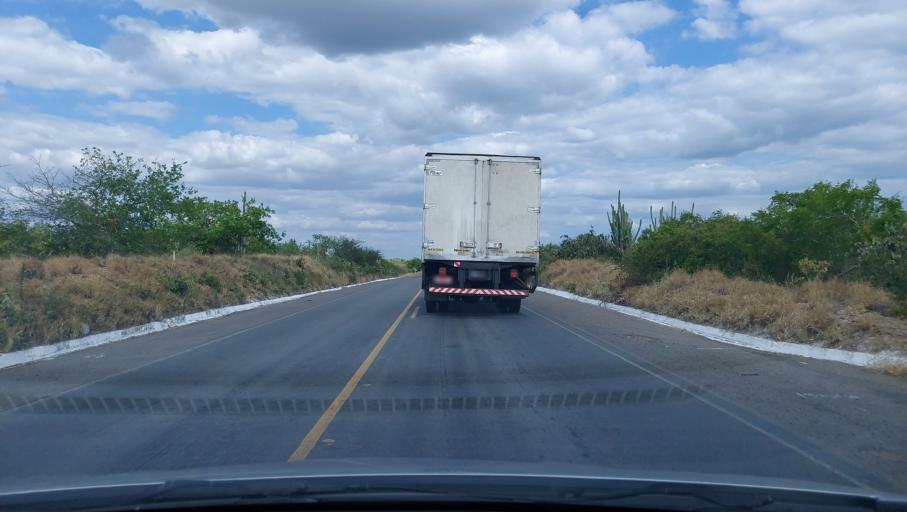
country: BR
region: Bahia
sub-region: Ipira
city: Ipira
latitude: -12.4983
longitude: -39.8488
